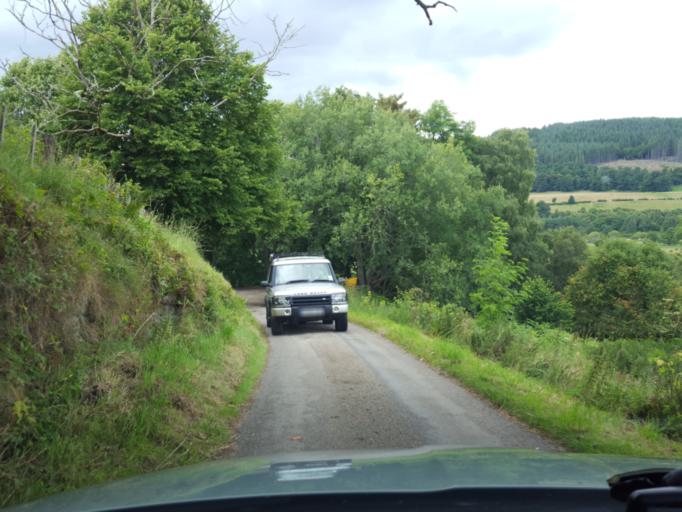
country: GB
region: Scotland
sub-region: Moray
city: Rothes
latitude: 57.4215
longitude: -3.3602
